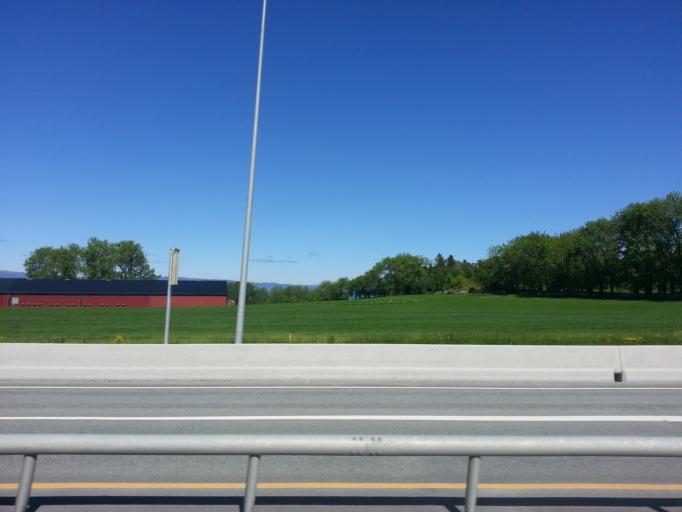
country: NO
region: Sor-Trondelag
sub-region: Trondheim
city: Trondheim
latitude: 63.4310
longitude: 10.4818
